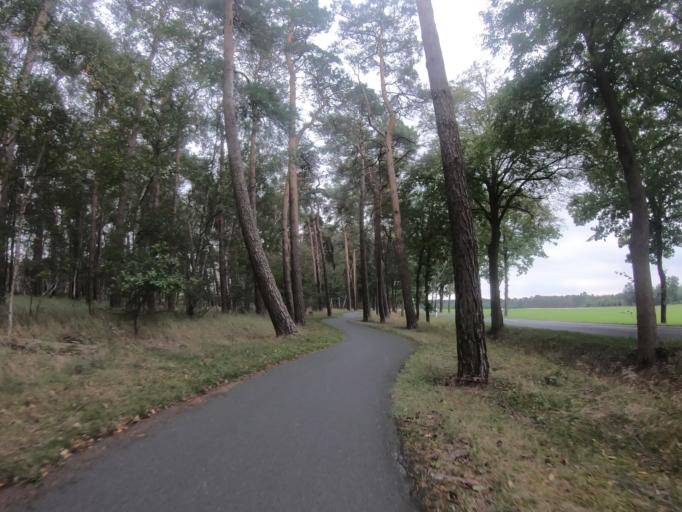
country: DE
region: Lower Saxony
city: Ribbesbuttel
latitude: 52.4437
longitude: 10.5024
